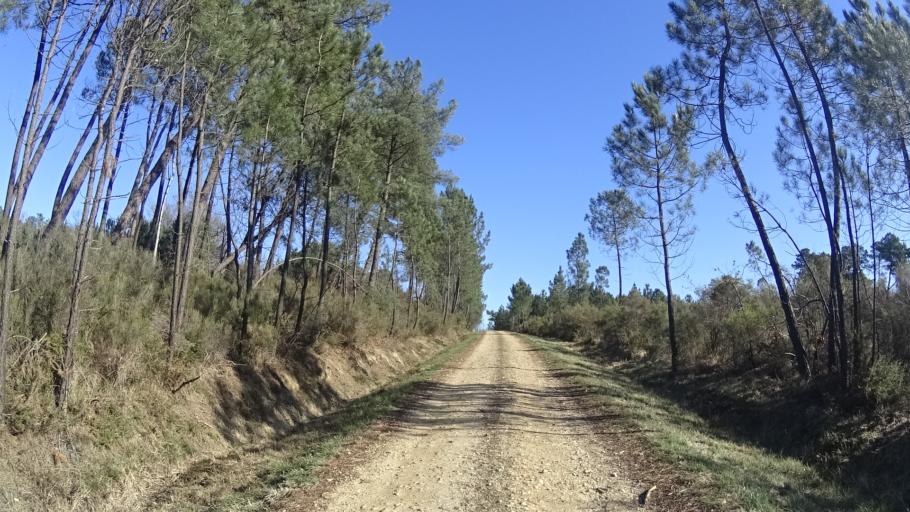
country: FR
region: Aquitaine
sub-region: Departement de la Dordogne
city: La Roche-Chalais
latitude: 45.2047
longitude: 0.0614
